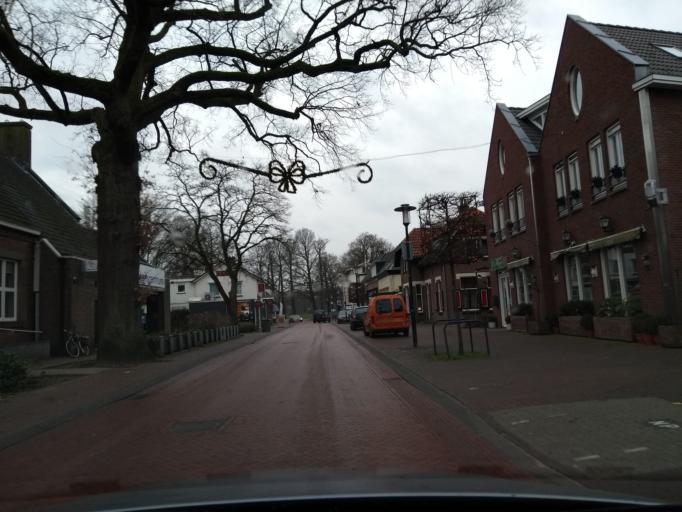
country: NL
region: Gelderland
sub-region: Gemeente Lochem
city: Barchem
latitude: 52.0856
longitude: 6.4496
